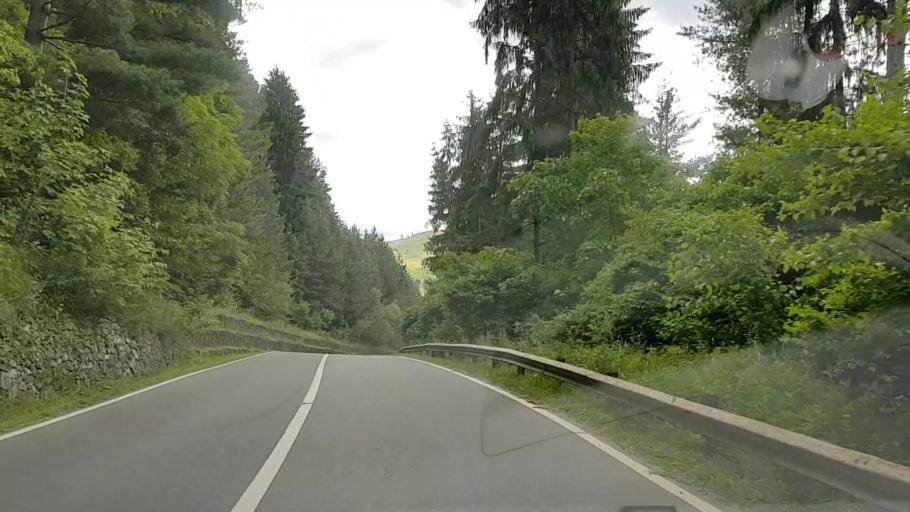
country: RO
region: Neamt
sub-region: Comuna Borca
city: Borca
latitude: 47.1760
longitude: 25.7923
